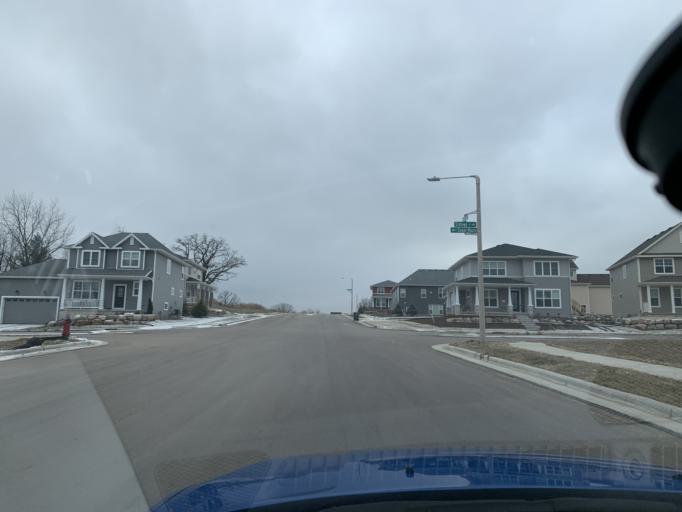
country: US
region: Wisconsin
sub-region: Dane County
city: Middleton
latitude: 43.0712
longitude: -89.5628
